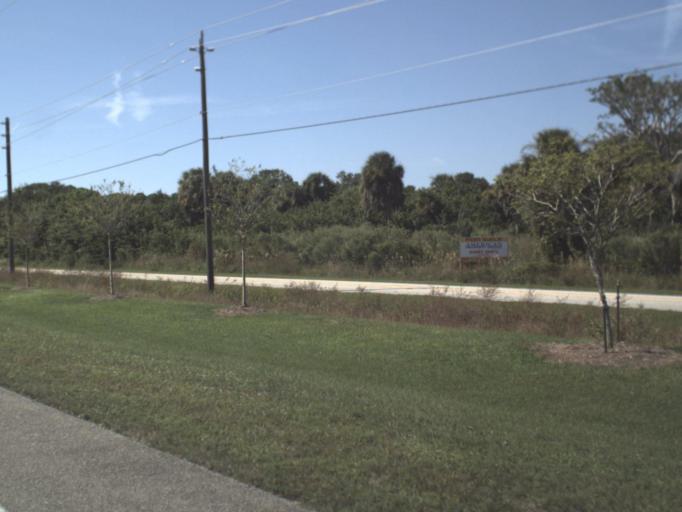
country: US
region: Florida
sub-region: Charlotte County
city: Grove City
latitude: 26.9346
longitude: -82.2981
